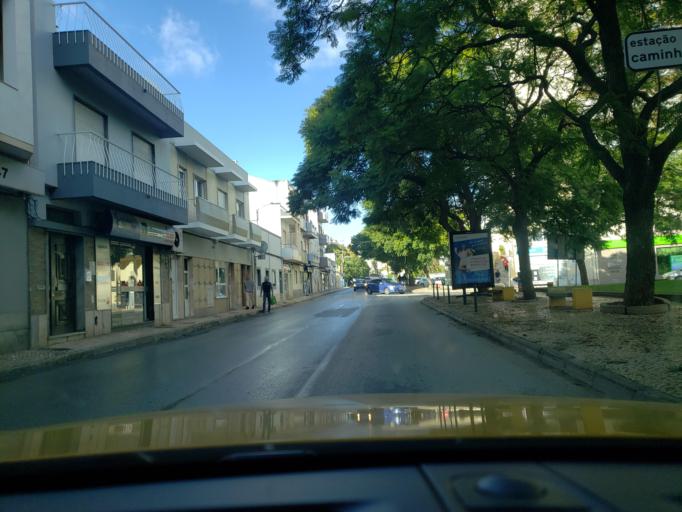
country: PT
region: Faro
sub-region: Portimao
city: Portimao
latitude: 37.1443
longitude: -8.5405
